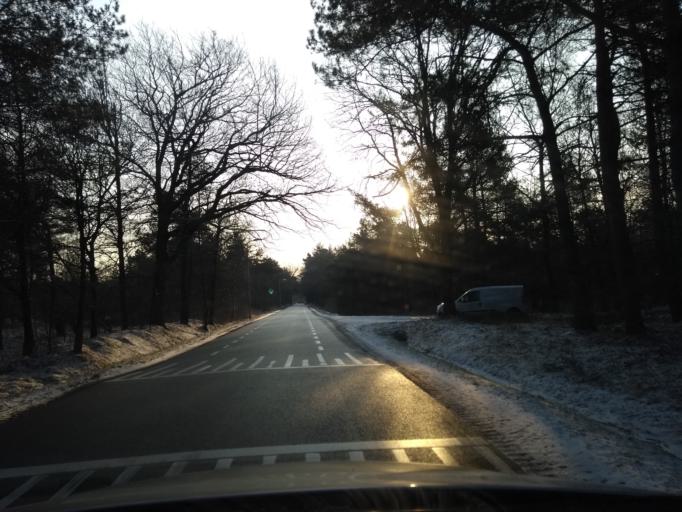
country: NL
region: Overijssel
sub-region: Gemeente Hof van Twente
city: Delden
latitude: 52.2197
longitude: 6.7147
